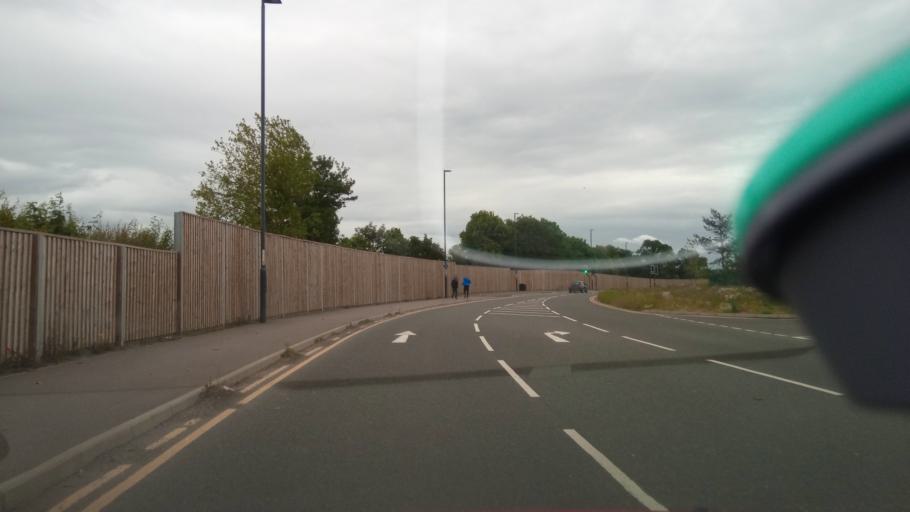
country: GB
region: England
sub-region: Derby
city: Derby
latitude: 52.8883
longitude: -1.4582
